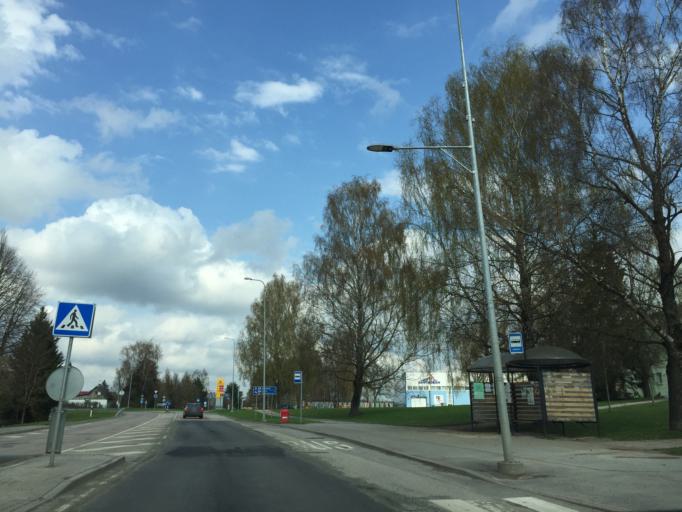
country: EE
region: Tartu
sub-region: Elva linn
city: Elva
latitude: 58.2345
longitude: 26.4105
